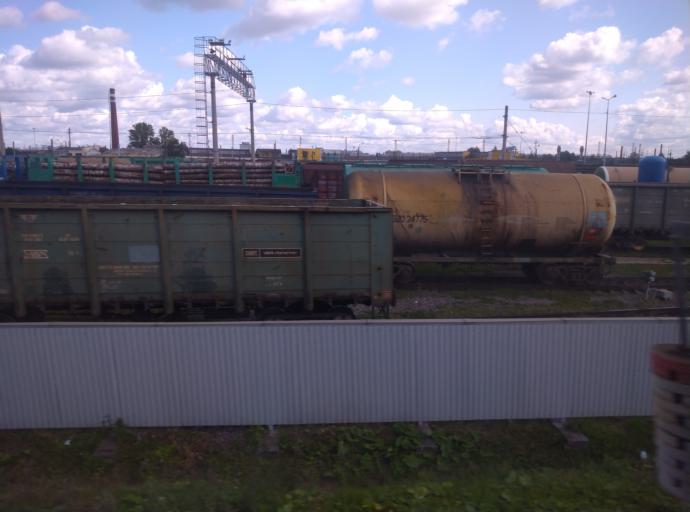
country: RU
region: St.-Petersburg
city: Obukhovo
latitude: 59.8700
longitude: 30.4199
